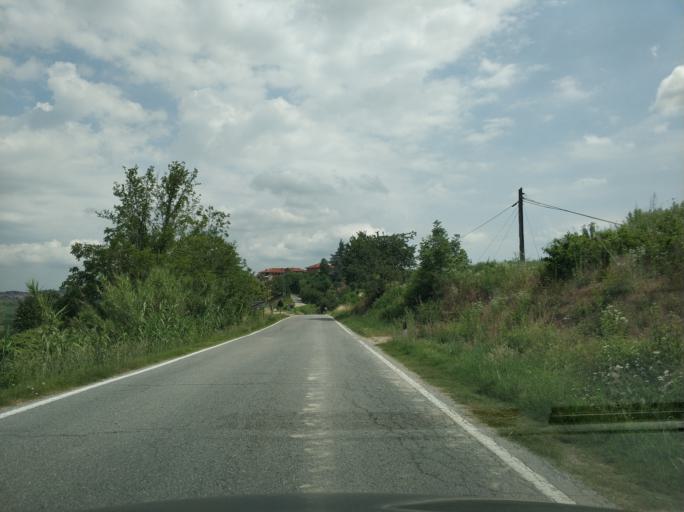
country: IT
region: Piedmont
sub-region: Provincia di Cuneo
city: Santo Stefano Roero
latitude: 44.7860
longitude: 7.9529
